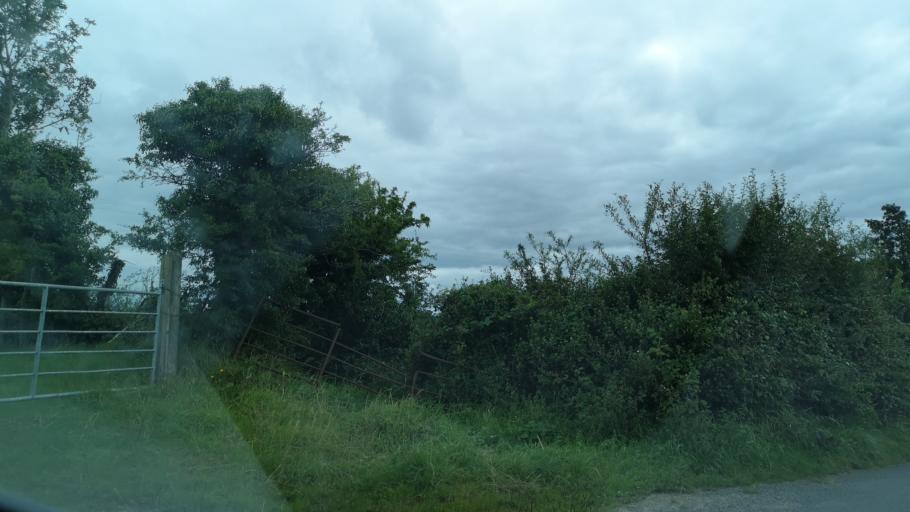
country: IE
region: Connaught
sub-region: County Galway
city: Loughrea
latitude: 53.1565
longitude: -8.4691
